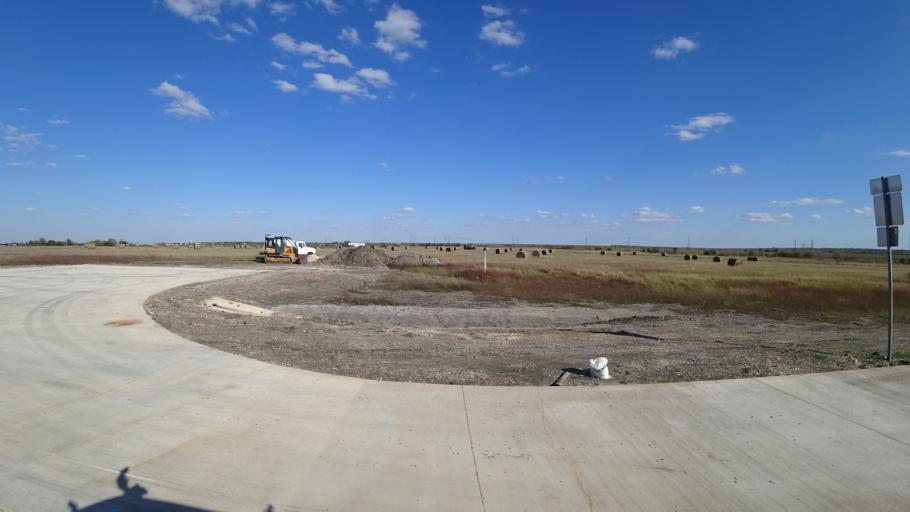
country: US
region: Texas
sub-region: Travis County
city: Onion Creek
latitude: 30.0923
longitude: -97.6938
